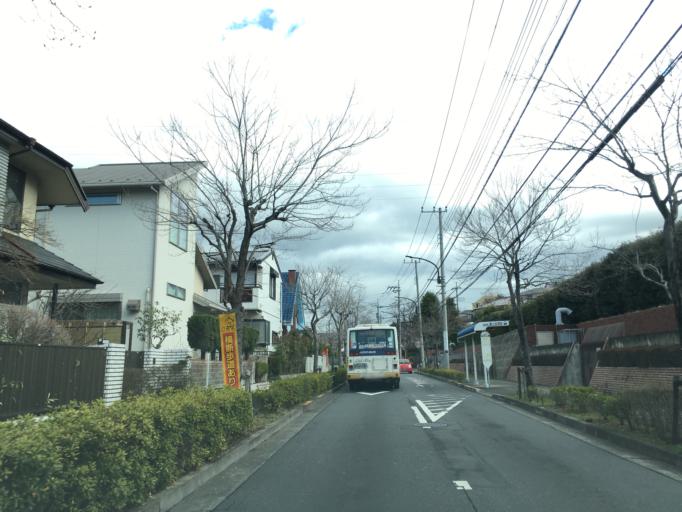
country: JP
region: Tokyo
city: Kokubunji
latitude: 35.6309
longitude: 139.4632
